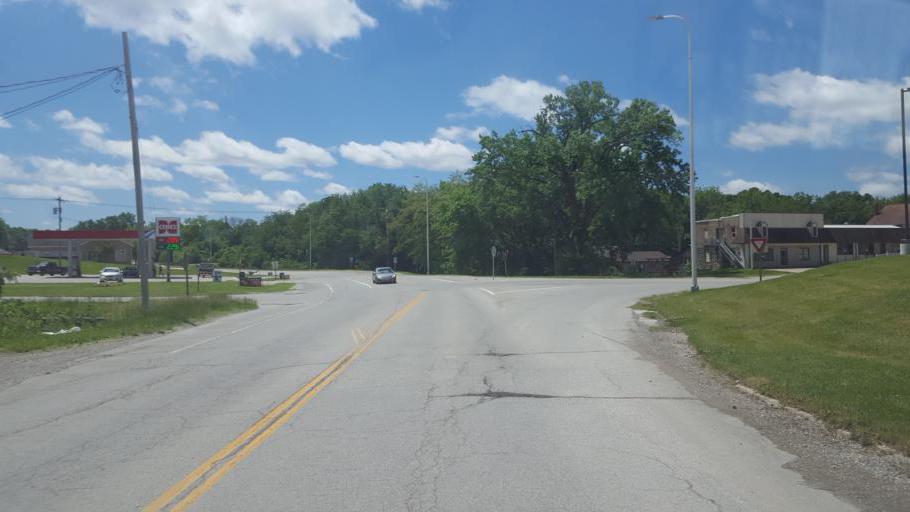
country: US
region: Missouri
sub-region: Harrison County
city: Bethany
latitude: 40.2691
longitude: -94.0276
